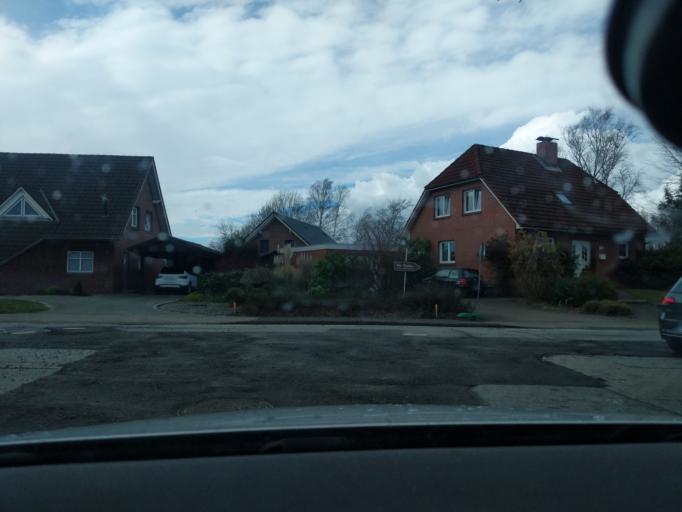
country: DE
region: Lower Saxony
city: Stade
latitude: 53.6110
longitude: 9.4739
